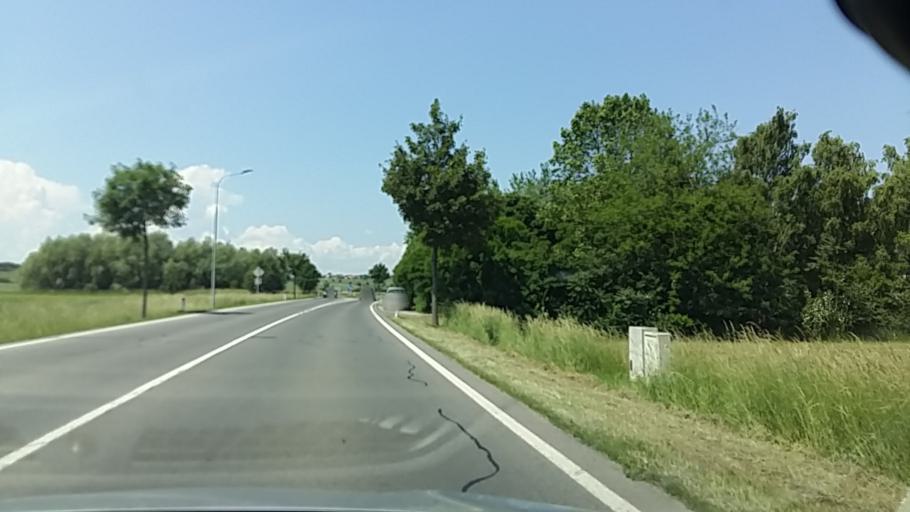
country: AT
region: Burgenland
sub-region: Politischer Bezirk Oberpullendorf
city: Horitschon
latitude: 47.5904
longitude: 16.5774
